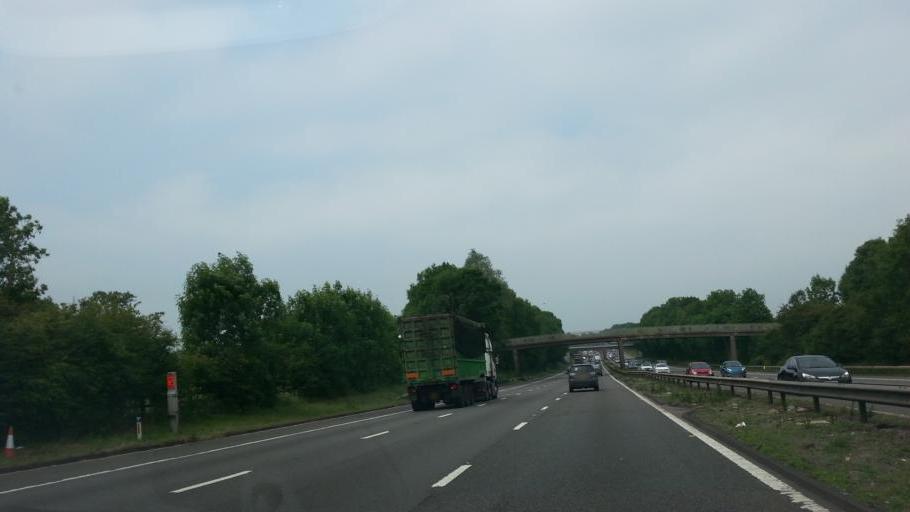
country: GB
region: England
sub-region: Staffordshire
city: Stafford
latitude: 52.7705
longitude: -2.1143
